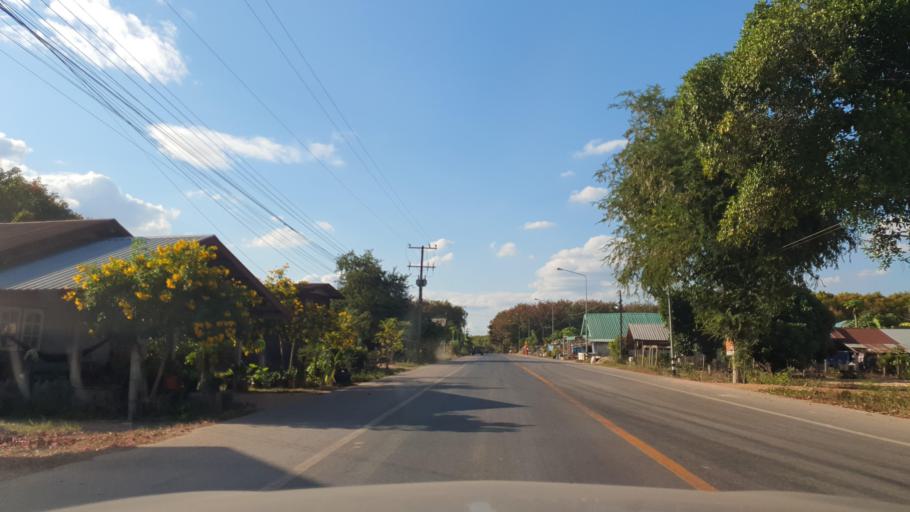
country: TH
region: Nong Khai
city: Bueng Khong Long
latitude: 18.0122
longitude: 104.0058
